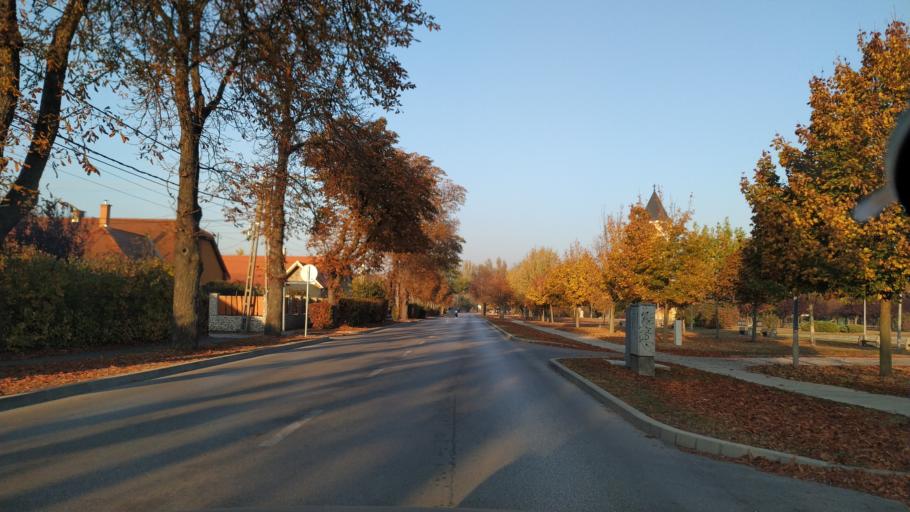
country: HU
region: Komarom-Esztergom
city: Dorog
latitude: 47.7268
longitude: 18.7329
